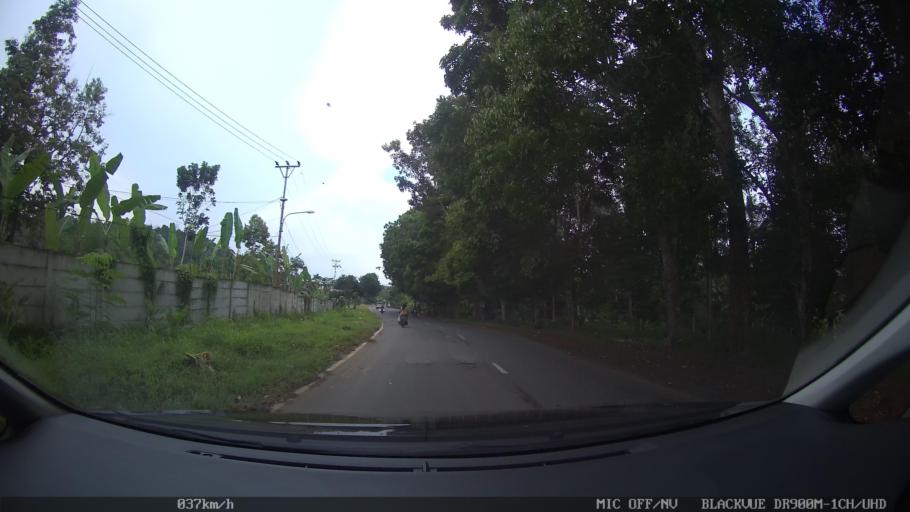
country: ID
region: Lampung
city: Bandarlampung
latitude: -5.4306
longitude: 105.2047
